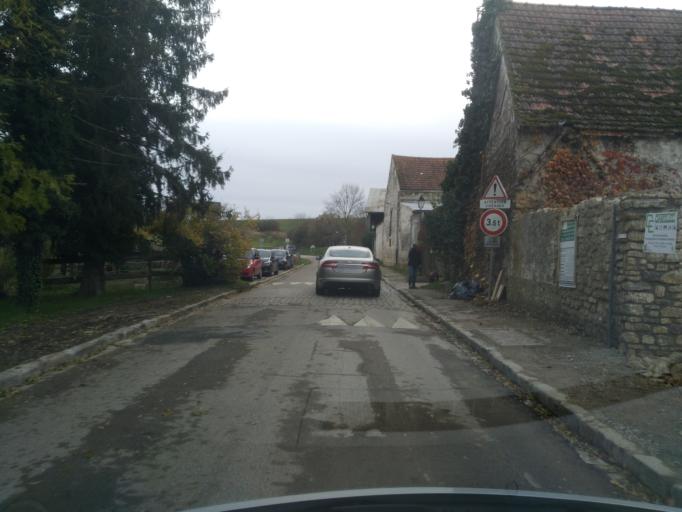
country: FR
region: Ile-de-France
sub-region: Departement des Yvelines
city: Chavenay
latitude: 48.8510
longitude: 1.9853
